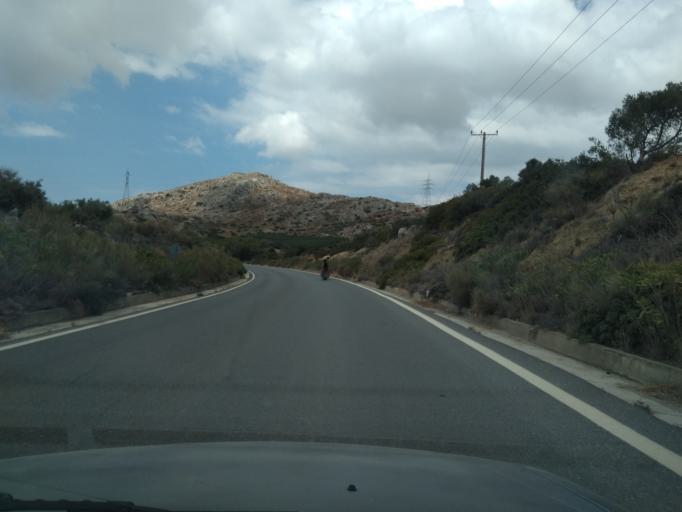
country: GR
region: Crete
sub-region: Nomos Lasithiou
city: Makry-Gialos
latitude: 35.0591
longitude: 26.0375
